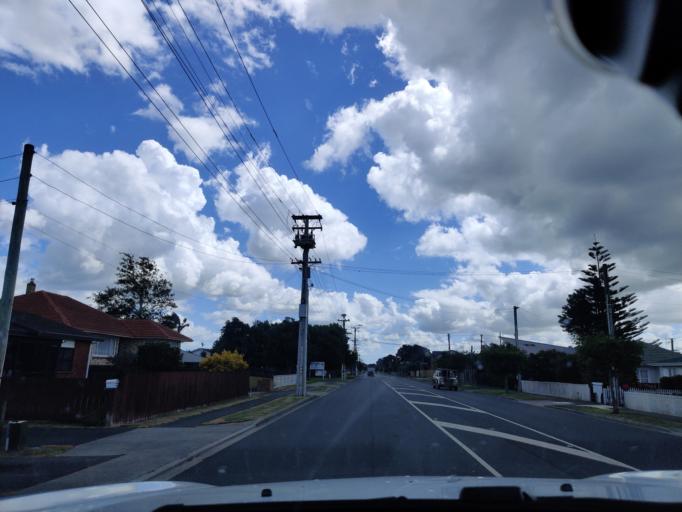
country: NZ
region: Auckland
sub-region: Auckland
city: Red Hill
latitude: -37.0561
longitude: 174.9571
